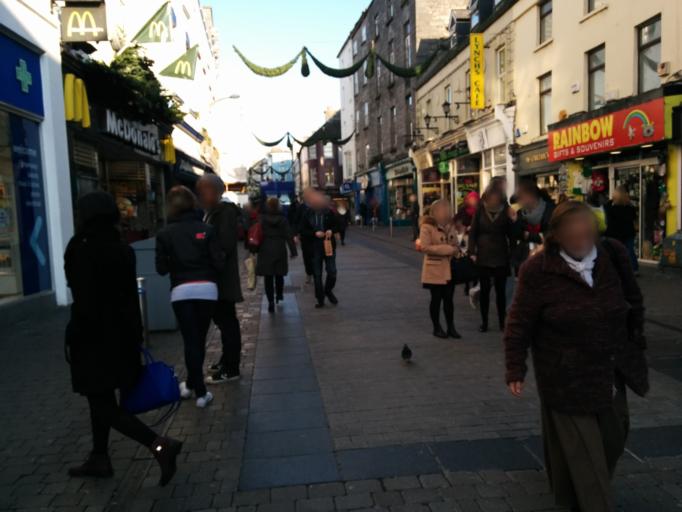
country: IE
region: Connaught
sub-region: County Galway
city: Gaillimh
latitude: 53.2728
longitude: -9.0526
